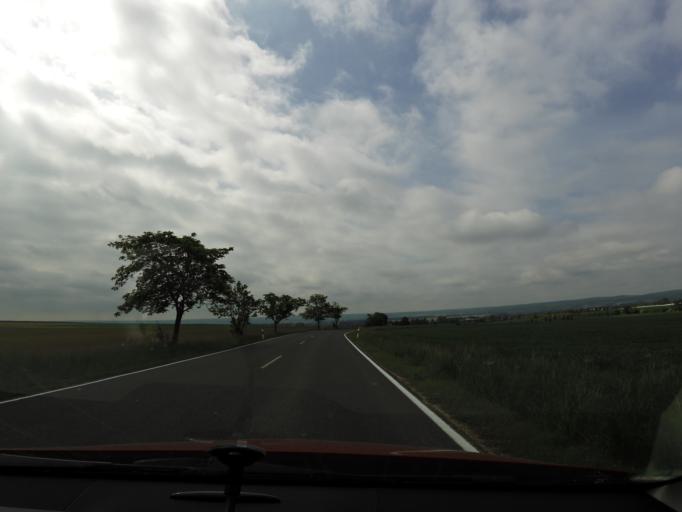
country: DE
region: Thuringia
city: Niederdorla
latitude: 51.1791
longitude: 10.4472
